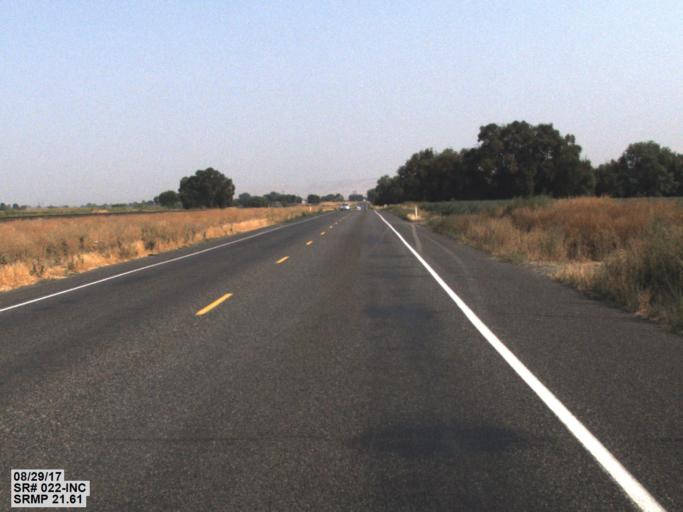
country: US
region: Washington
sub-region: Yakima County
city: Mabton
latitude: 46.2189
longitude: -120.0293
